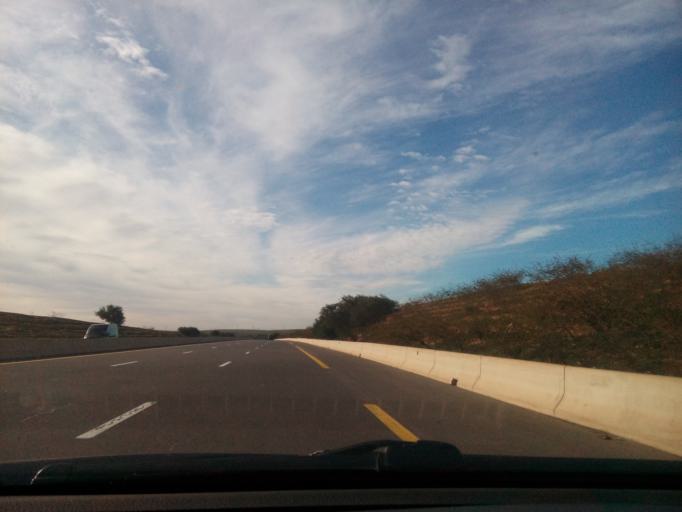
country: DZ
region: Sidi Bel Abbes
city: Sidi Bel Abbes
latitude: 35.1671
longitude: -0.7668
